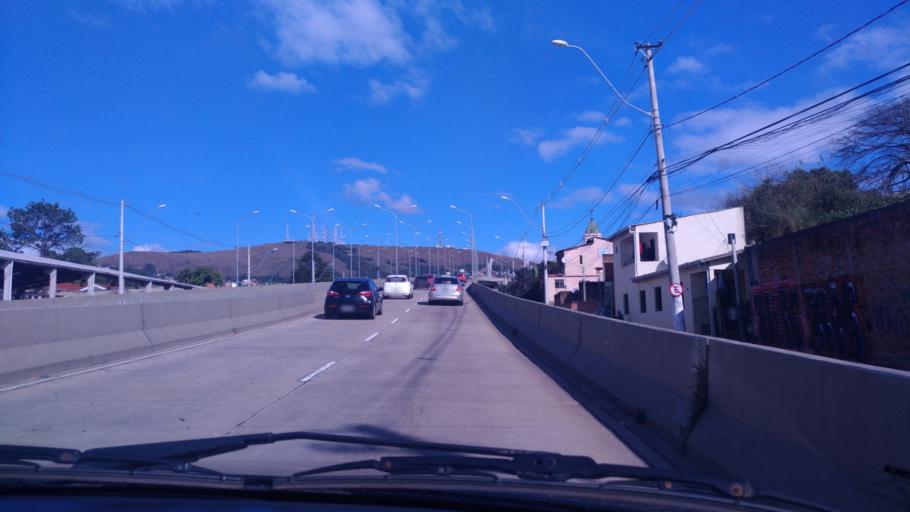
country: BR
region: Rio Grande do Sul
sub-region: Porto Alegre
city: Porto Alegre
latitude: -30.0607
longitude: -51.1849
